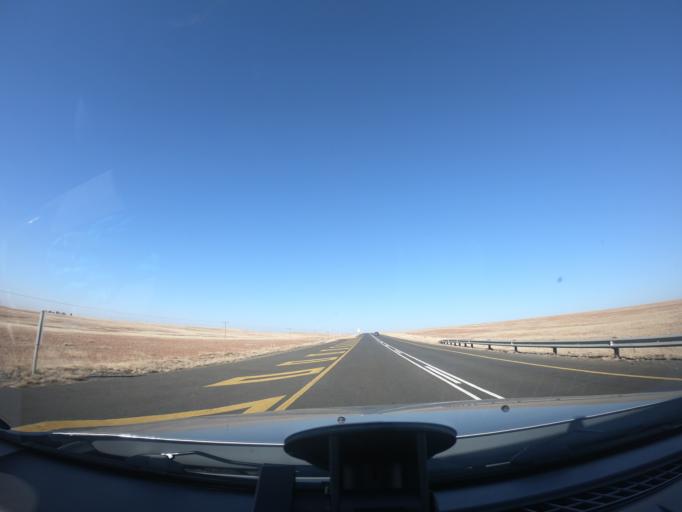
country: ZA
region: Mpumalanga
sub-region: Gert Sibande District Municipality
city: Ermelo
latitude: -26.8284
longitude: 29.9226
